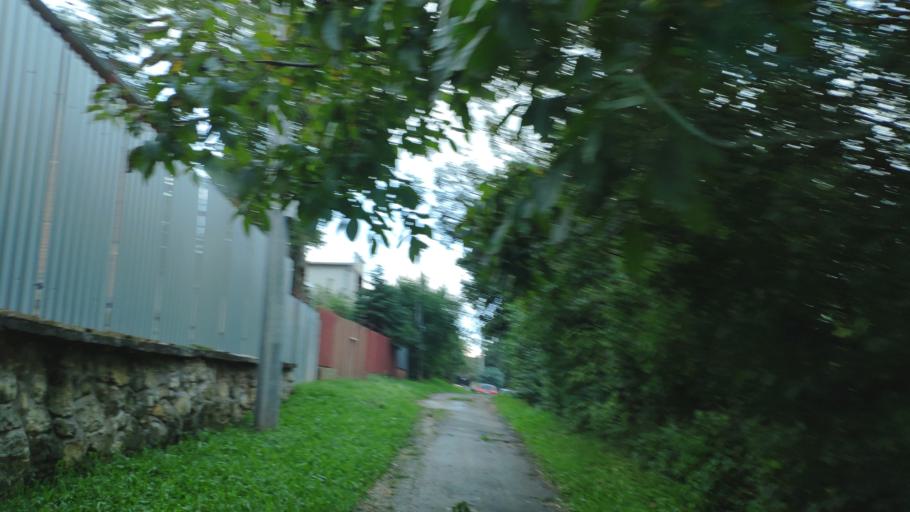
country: SK
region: Kosicky
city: Moldava nad Bodvou
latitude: 48.5859
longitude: 20.9237
